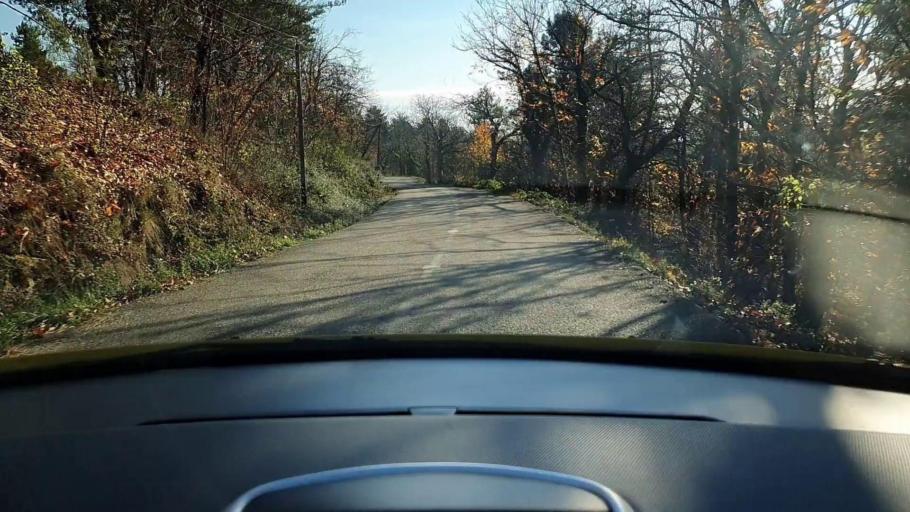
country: FR
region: Languedoc-Roussillon
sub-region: Departement du Gard
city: Branoux-les-Taillades
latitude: 44.2830
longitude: 3.9456
